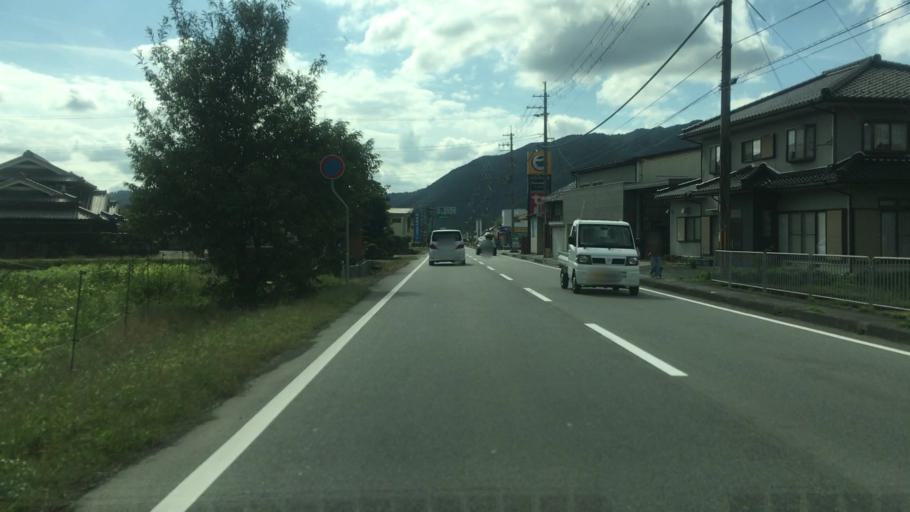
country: JP
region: Kyoto
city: Fukuchiyama
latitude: 35.2466
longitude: 135.0067
